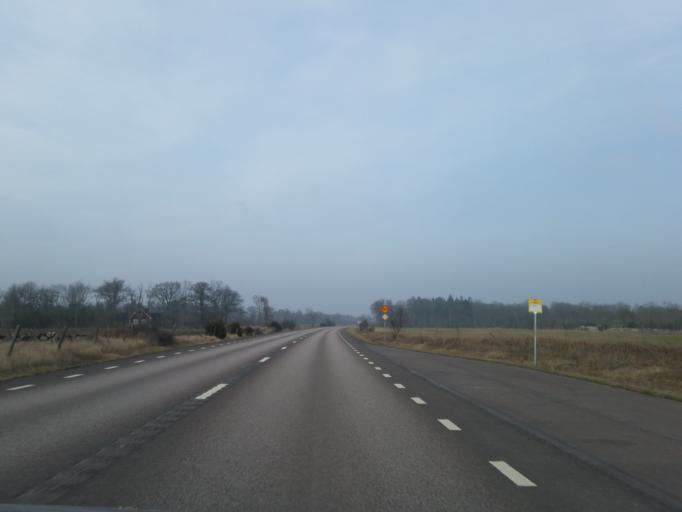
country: SE
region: Kalmar
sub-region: Borgholms Kommun
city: Borgholm
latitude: 57.1021
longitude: 16.9355
